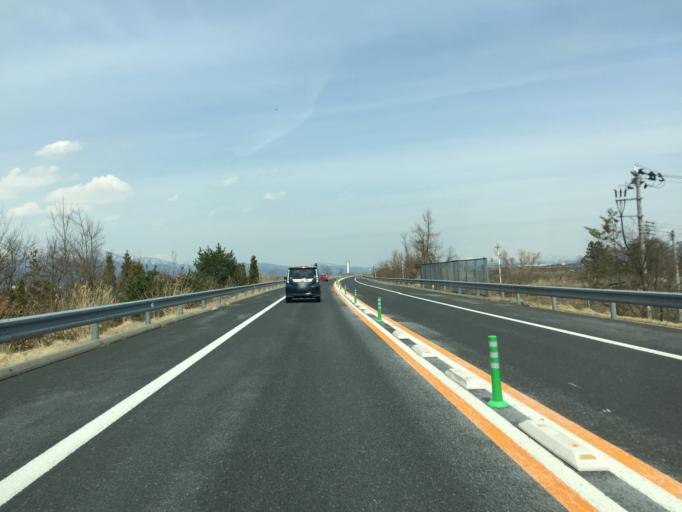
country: JP
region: Yamagata
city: Tendo
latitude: 38.3914
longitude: 140.3428
